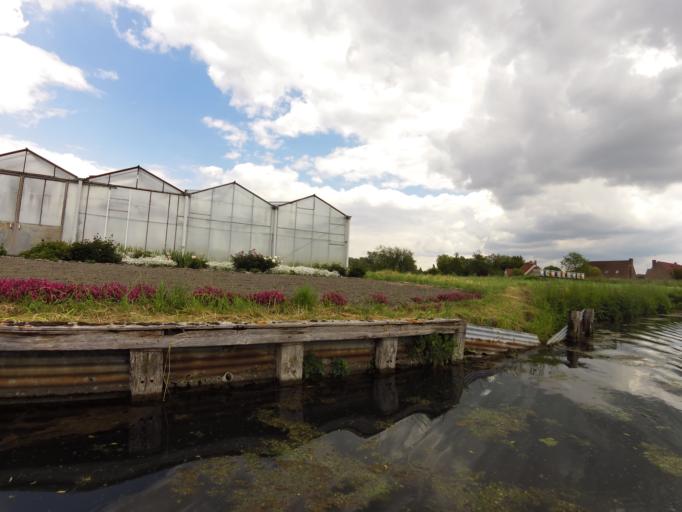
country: FR
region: Nord-Pas-de-Calais
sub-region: Departement du Pas-de-Calais
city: Saint-Martin-au-Laert
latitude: 50.7603
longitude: 2.2452
